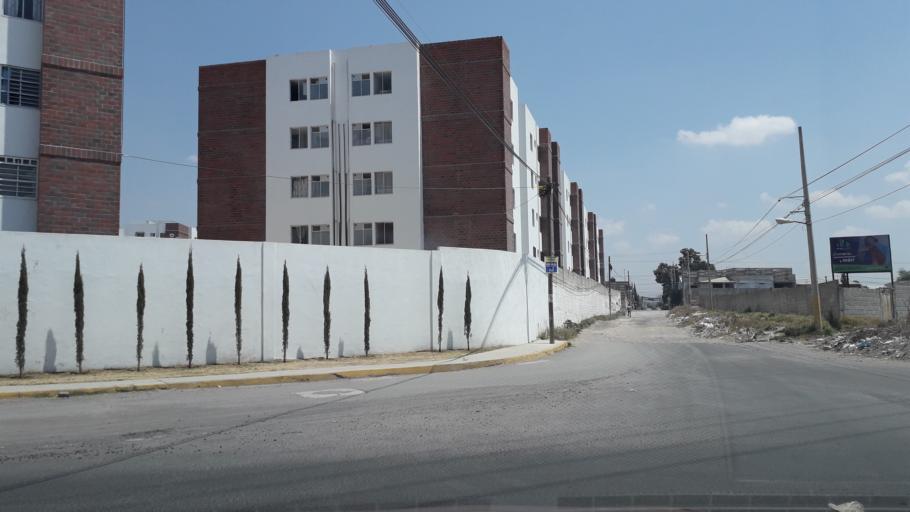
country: MX
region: Puebla
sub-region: Amozoc
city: Casa Blanca
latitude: 19.0614
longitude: -98.1209
